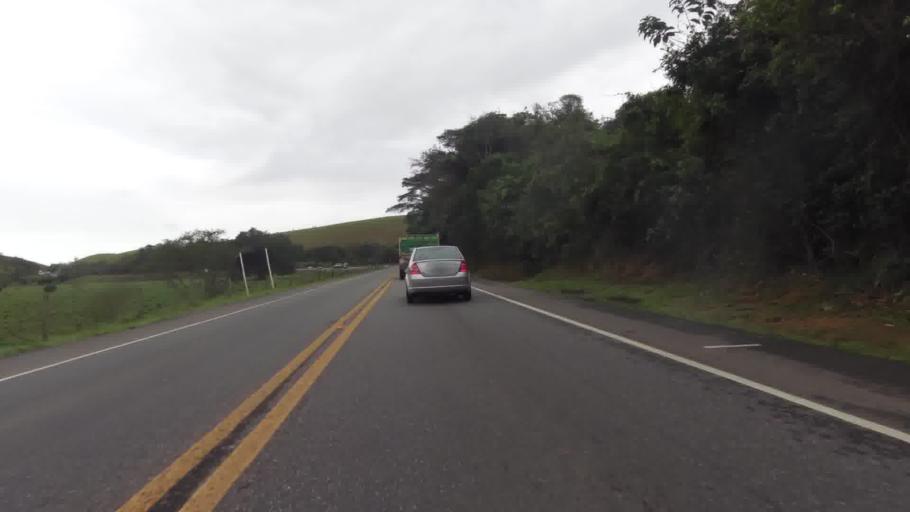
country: BR
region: Espirito Santo
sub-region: Rio Novo Do Sul
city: Rio Novo do Sul
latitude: -20.8515
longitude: -40.8773
